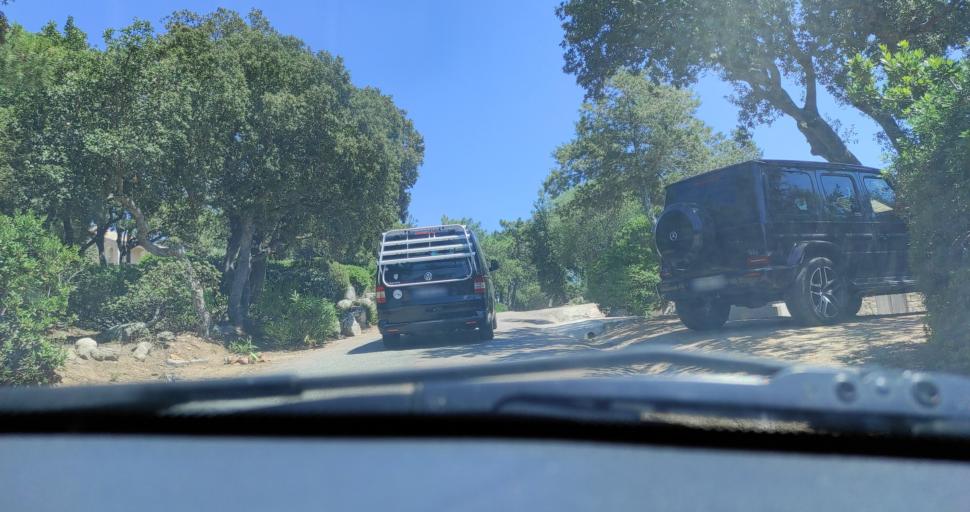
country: FR
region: Corsica
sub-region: Departement de la Corse-du-Sud
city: Porto-Vecchio
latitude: 41.6208
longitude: 9.3417
